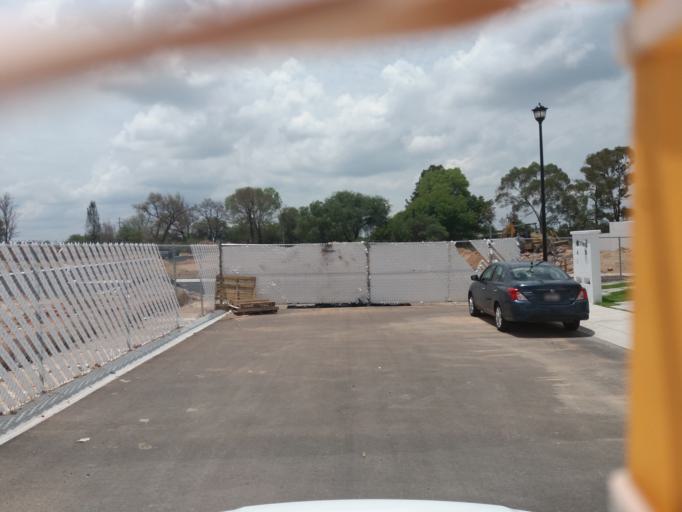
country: MX
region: Aguascalientes
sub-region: Aguascalientes
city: San Sebastian [Fraccionamiento]
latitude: 21.8049
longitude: -102.2655
